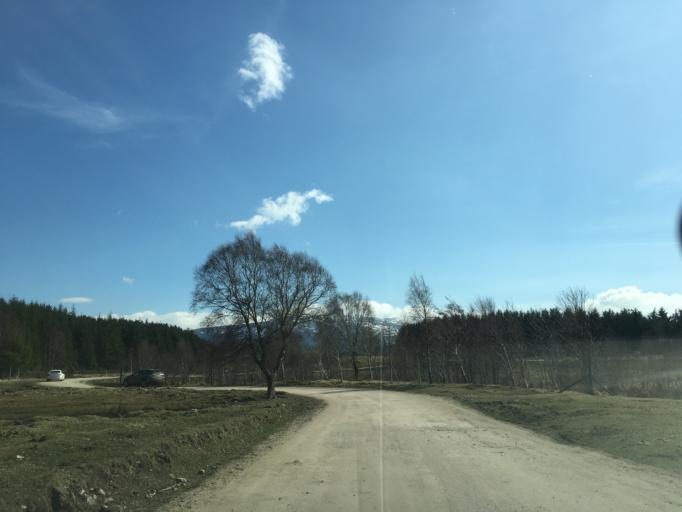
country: GB
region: Scotland
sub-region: Highland
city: Kingussie
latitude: 57.1119
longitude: -3.9743
